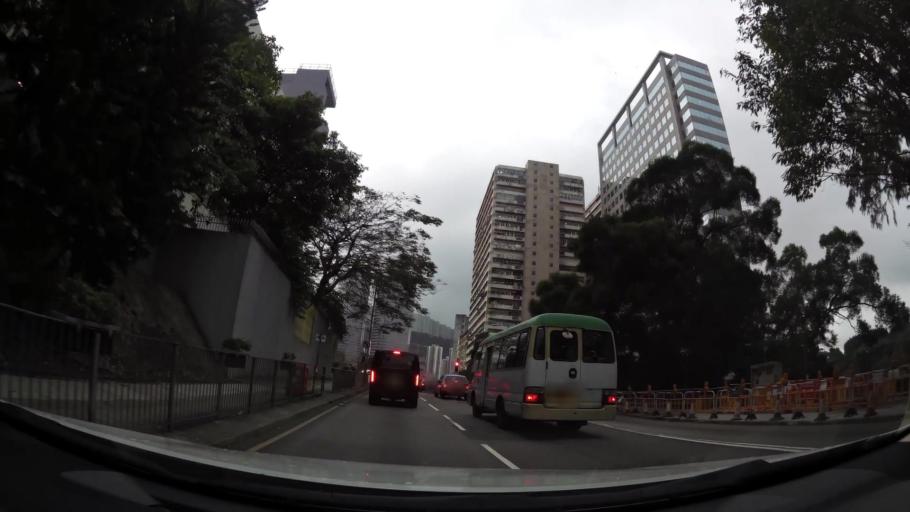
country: HK
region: Tsuen Wan
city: Tsuen Wan
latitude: 22.3591
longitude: 114.1212
